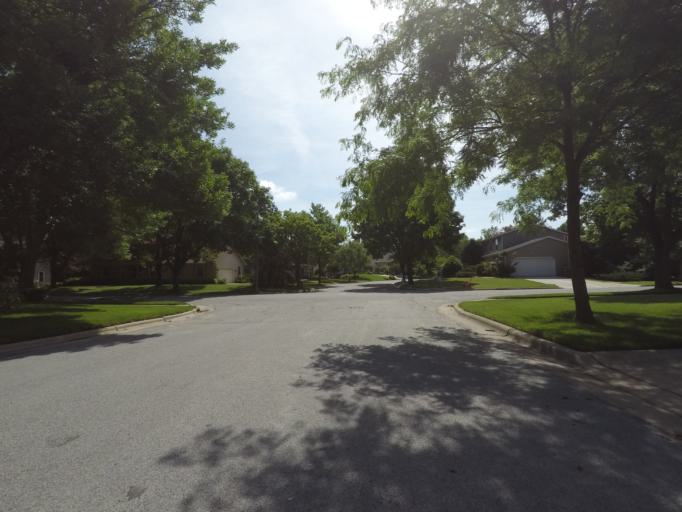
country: US
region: Wisconsin
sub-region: Dane County
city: Middleton
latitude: 43.0832
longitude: -89.5140
